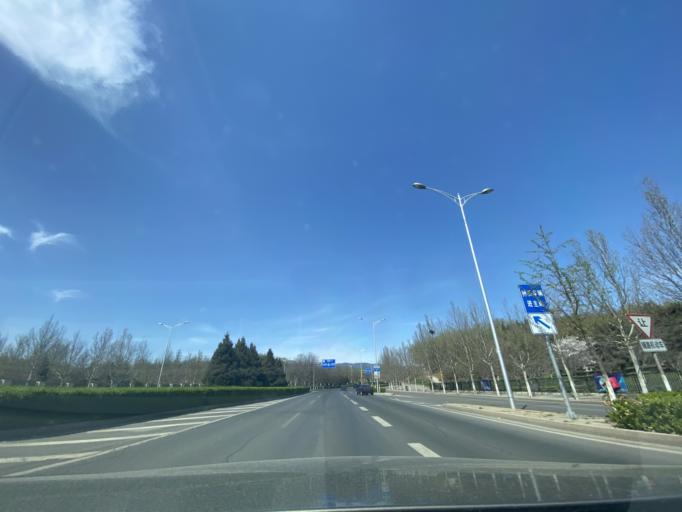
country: CN
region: Beijing
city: Sijiqing
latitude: 39.9372
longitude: 116.2418
